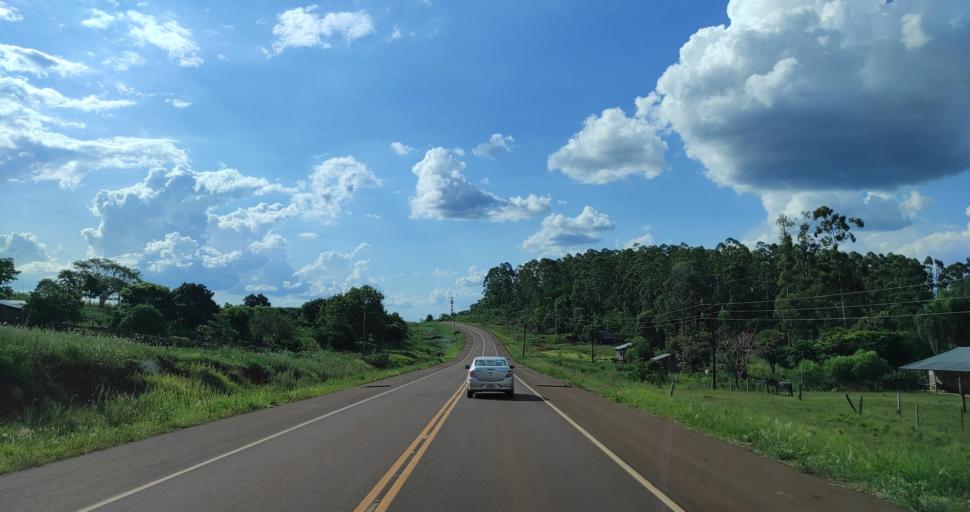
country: AR
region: Misiones
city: Bernardo de Irigoyen
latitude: -26.3810
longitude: -53.9170
